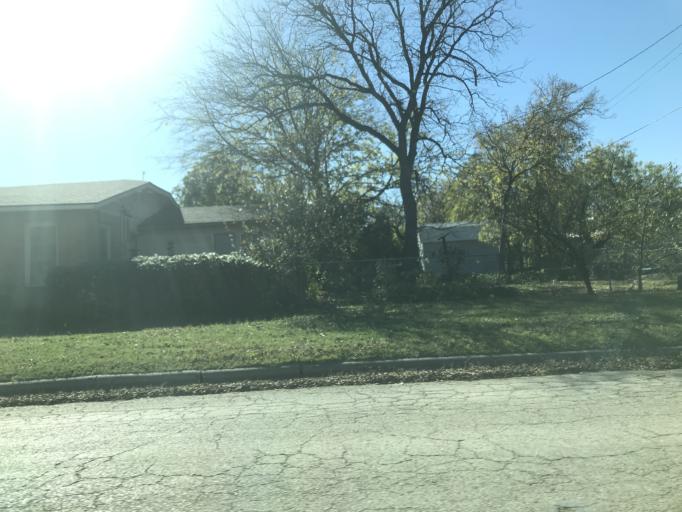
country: US
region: Texas
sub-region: Taylor County
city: Abilene
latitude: 32.4640
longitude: -99.7358
